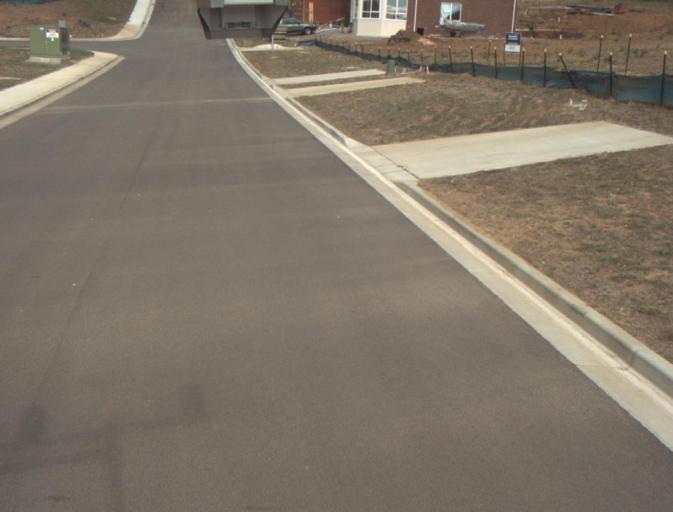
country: AU
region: Tasmania
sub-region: Launceston
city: Newstead
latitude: -41.4521
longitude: 147.1685
